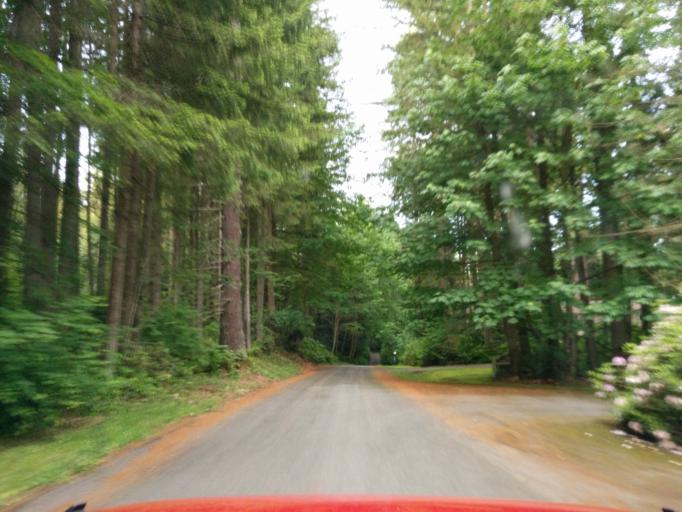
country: US
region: Washington
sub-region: King County
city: Union Hill-Novelty Hill
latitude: 47.6714
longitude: -122.0198
